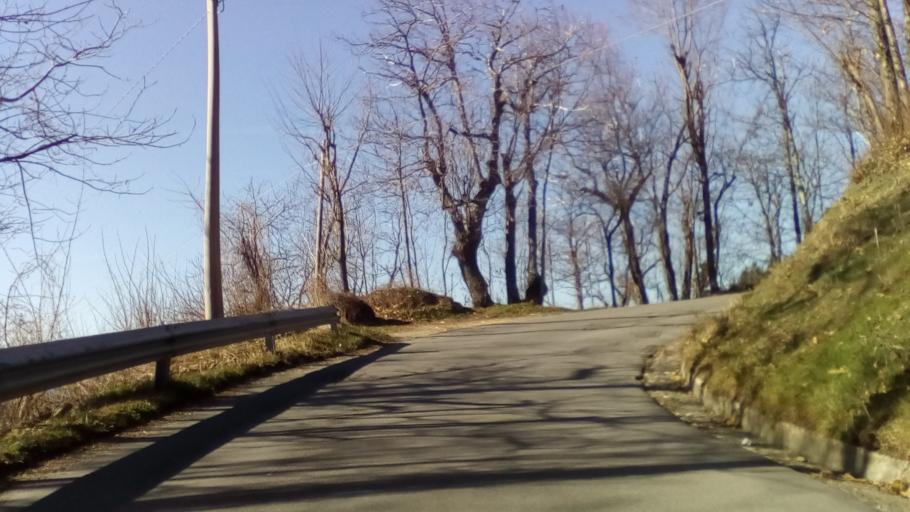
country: IT
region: Tuscany
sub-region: Provincia di Lucca
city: Castiglione di Garfagnana
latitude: 44.1522
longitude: 10.4416
